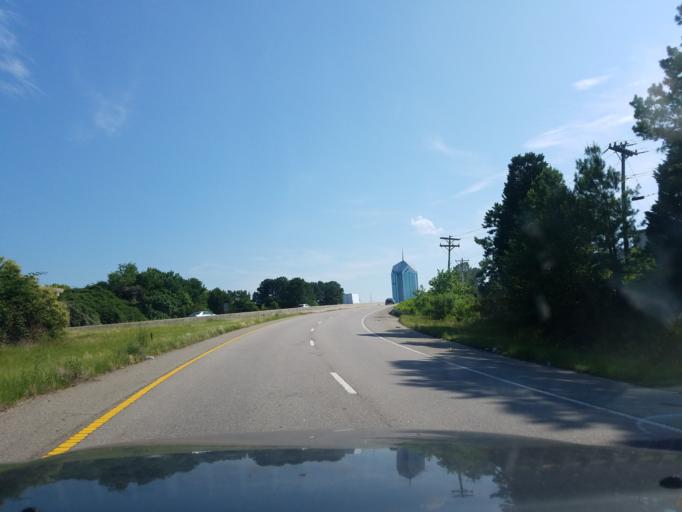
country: US
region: North Carolina
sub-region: Durham County
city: Durham
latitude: 35.9659
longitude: -78.9642
